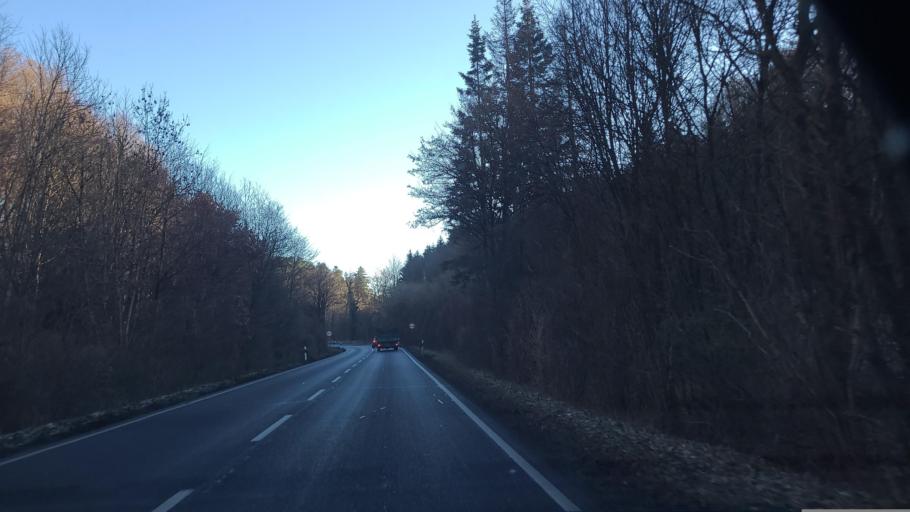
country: LU
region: Luxembourg
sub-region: Canton de Luxembourg
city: Strassen
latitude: 49.6328
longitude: 6.0868
